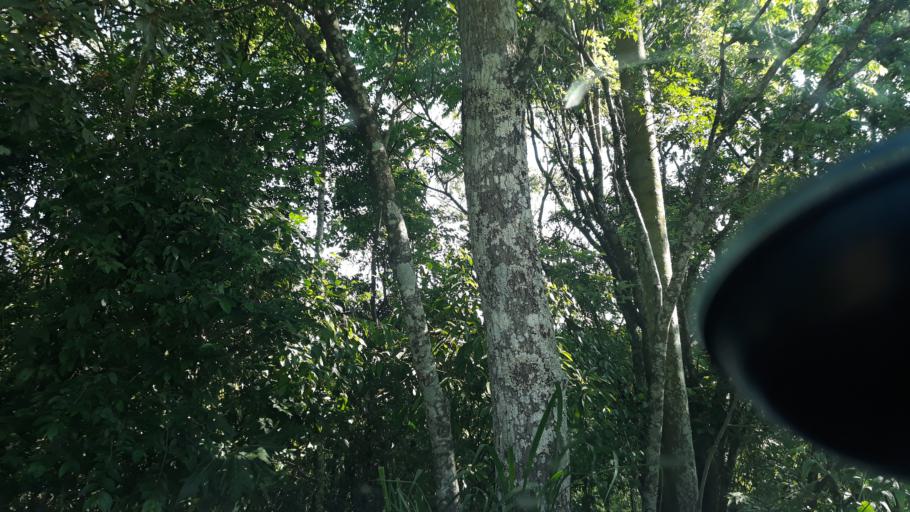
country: AR
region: Misiones
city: Bernardo de Irigoyen
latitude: -26.2708
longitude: -53.6674
